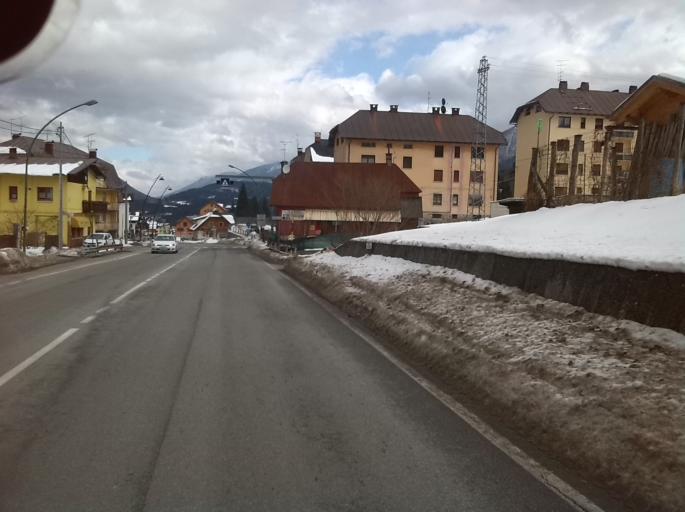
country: IT
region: Friuli Venezia Giulia
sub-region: Provincia di Udine
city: Tarvisio
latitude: 46.5066
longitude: 13.5597
